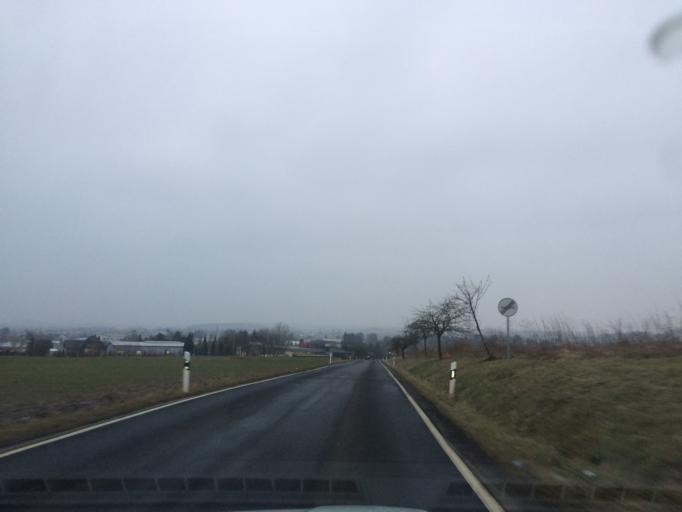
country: DE
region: Hesse
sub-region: Regierungsbezirk Kassel
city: Hofgeismar
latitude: 51.5105
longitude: 9.3882
